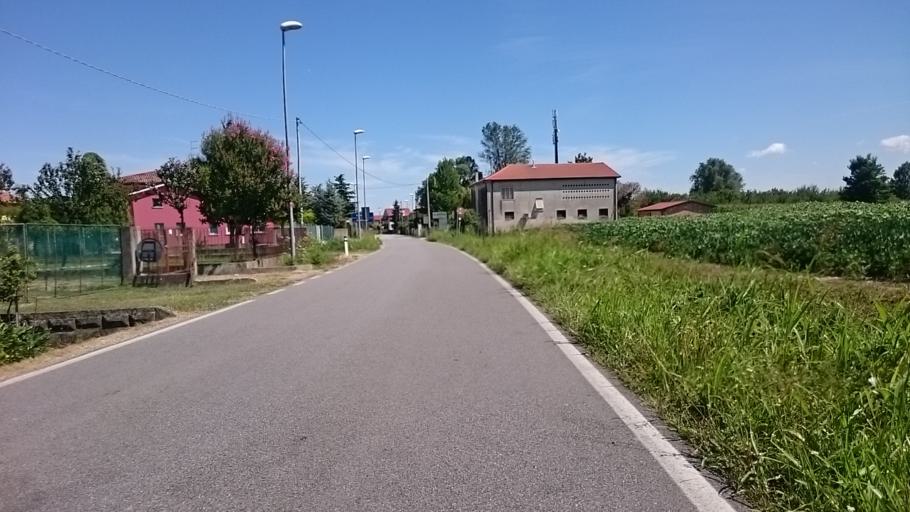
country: IT
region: Veneto
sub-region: Provincia di Venezia
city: Fiesso d'Artico
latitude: 45.4411
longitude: 12.0233
